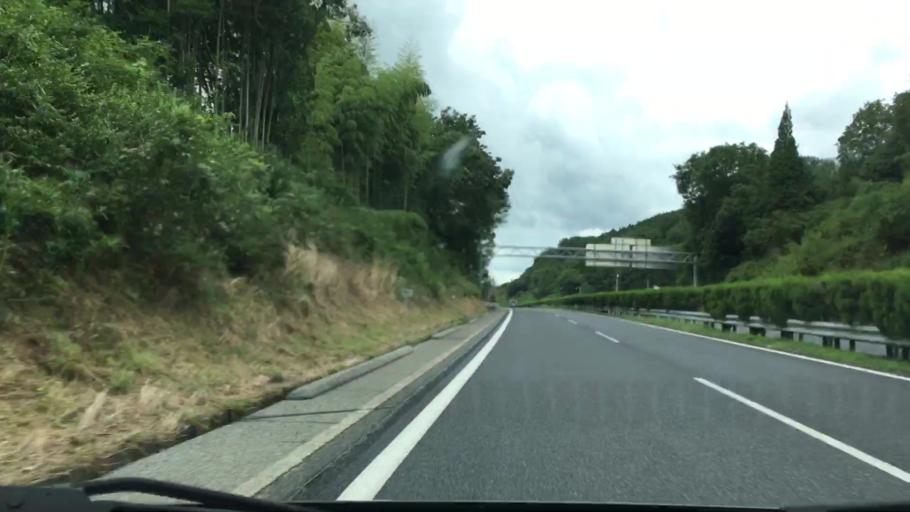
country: JP
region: Okayama
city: Tsuyama
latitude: 35.0406
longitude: 134.1259
